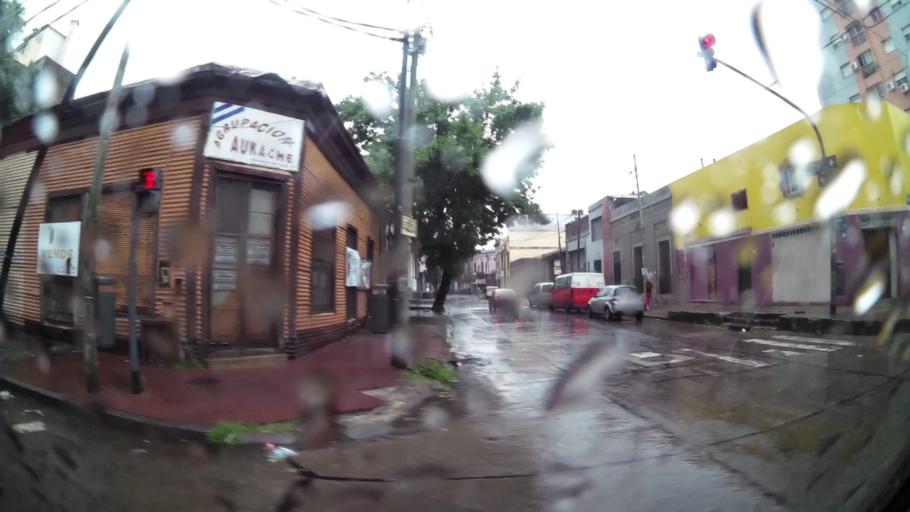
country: AR
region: Buenos Aires F.D.
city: Buenos Aires
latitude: -34.6322
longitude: -58.3590
